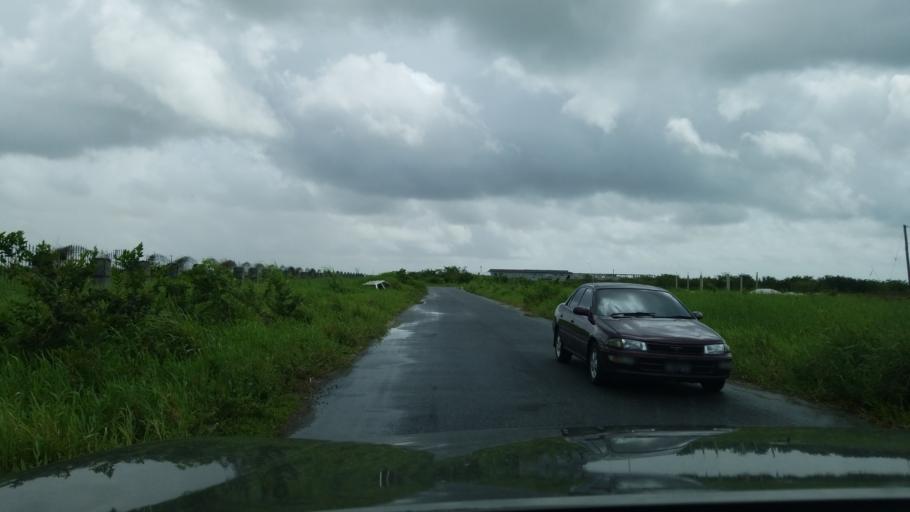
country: GY
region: Demerara-Mahaica
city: Georgetown
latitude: 6.7559
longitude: -58.1618
